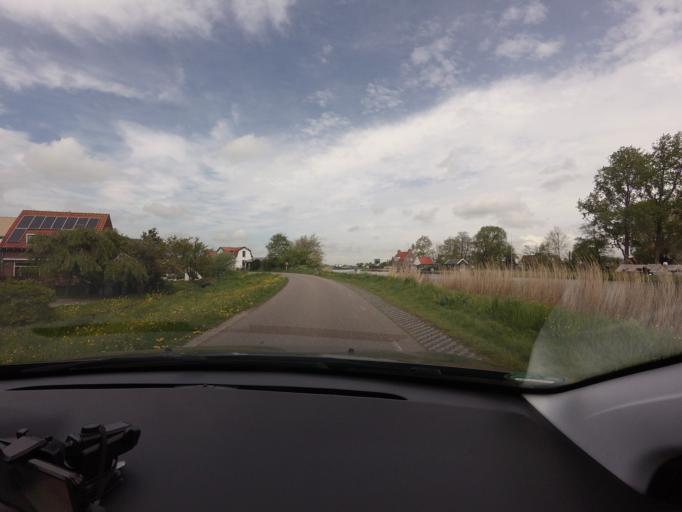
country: NL
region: North Holland
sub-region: Gemeente Zaanstad
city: Zaanstad
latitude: 52.5376
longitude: 4.8347
